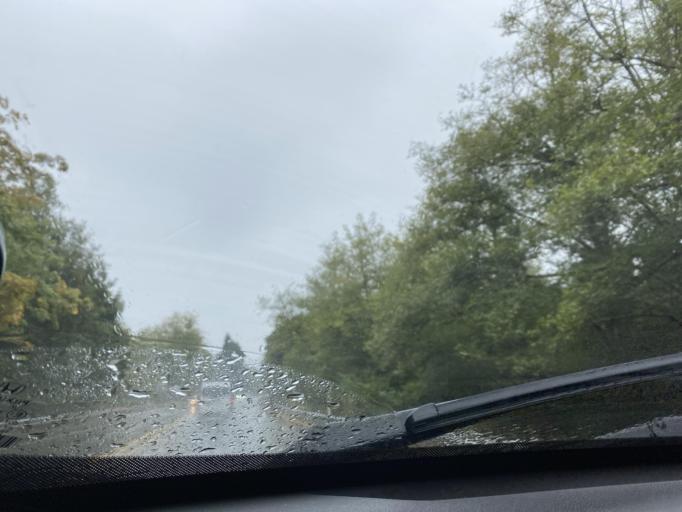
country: US
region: Washington
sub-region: Kitsap County
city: Bainbridge Island
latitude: 47.6739
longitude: -122.5335
